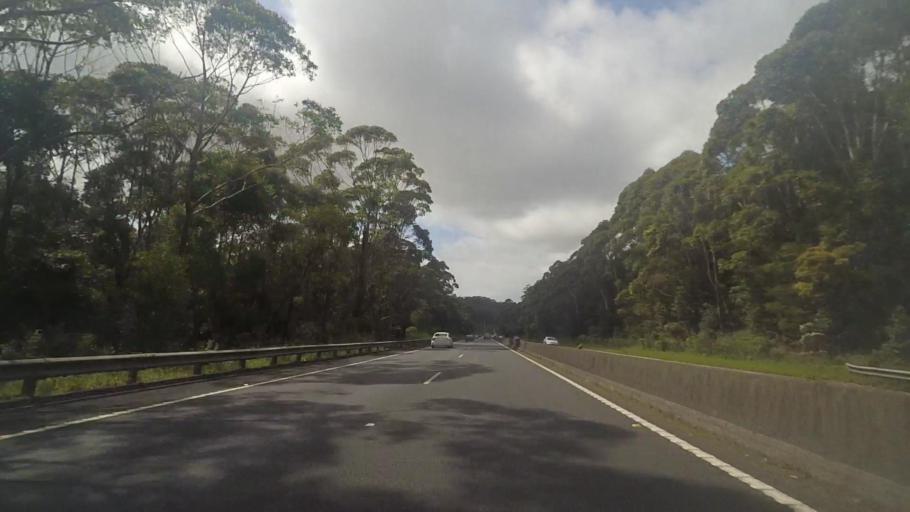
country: AU
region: New South Wales
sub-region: Wollongong
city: Bulli
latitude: -34.3312
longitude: 150.8780
